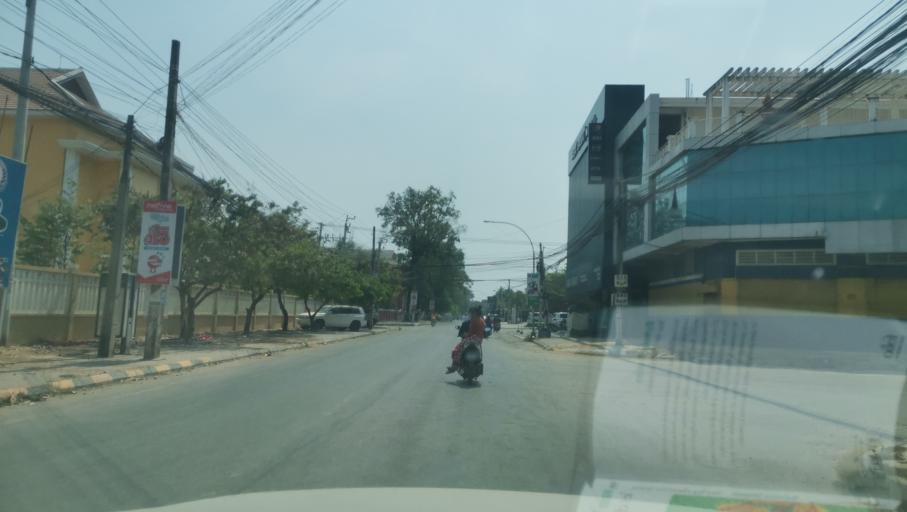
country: KH
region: Battambang
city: Battambang
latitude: 13.0916
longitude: 103.1969
